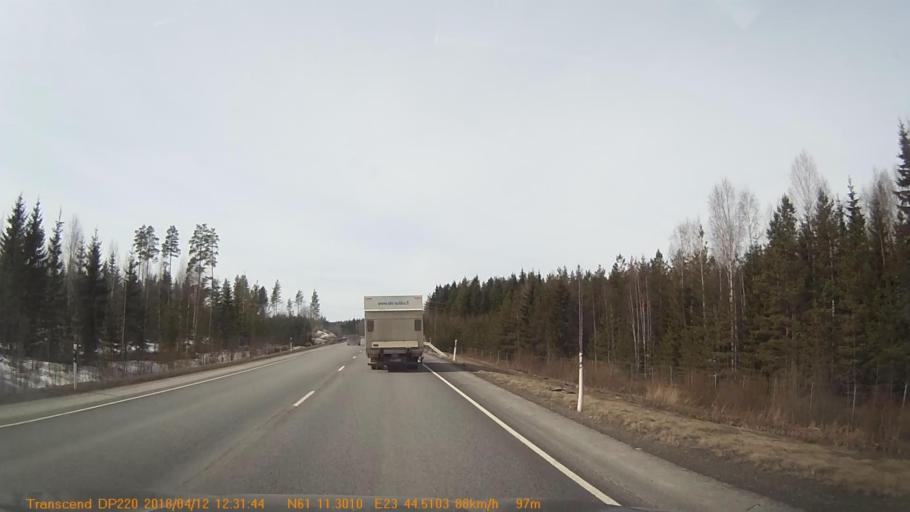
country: FI
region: Pirkanmaa
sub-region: Etelae-Pirkanmaa
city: Viiala
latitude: 61.1884
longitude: 23.7411
